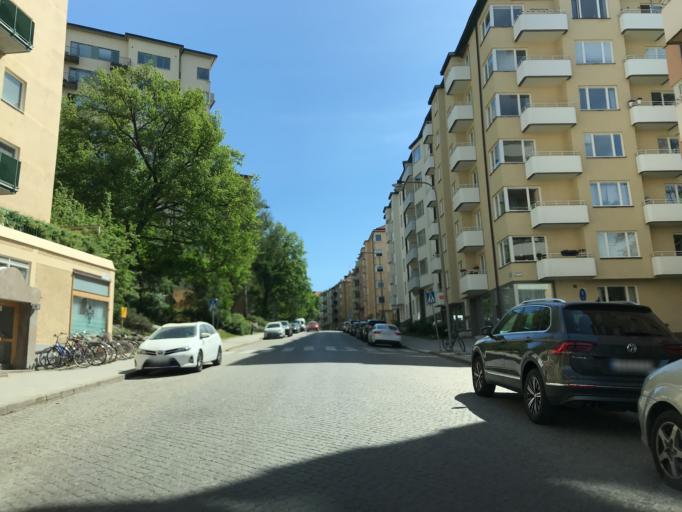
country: SE
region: Stockholm
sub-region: Stockholms Kommun
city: OEstermalm
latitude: 59.3475
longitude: 18.0947
